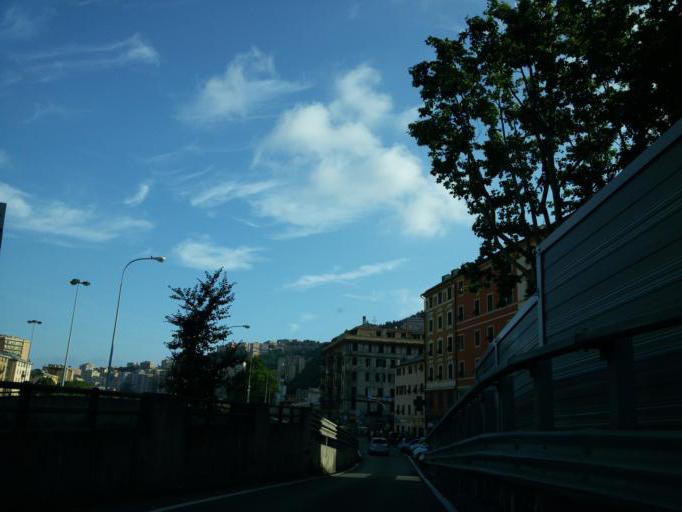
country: IT
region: Liguria
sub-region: Provincia di Genova
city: Genoa
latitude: 44.4265
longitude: 8.9478
